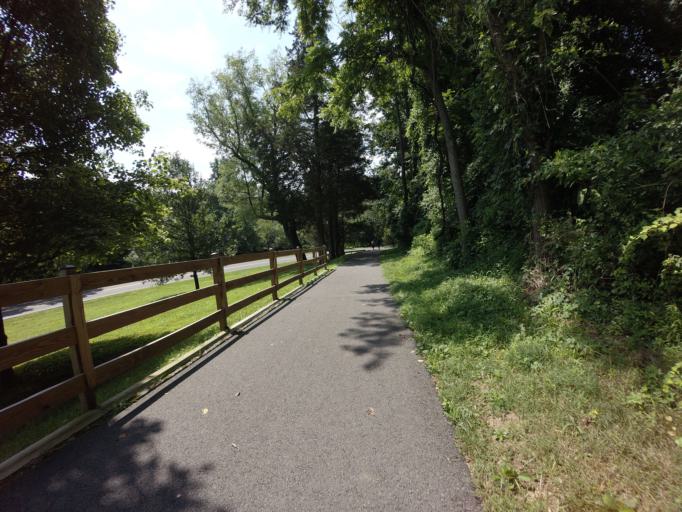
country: US
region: Maryland
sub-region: Montgomery County
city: Forest Glen
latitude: 39.0091
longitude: -77.0682
